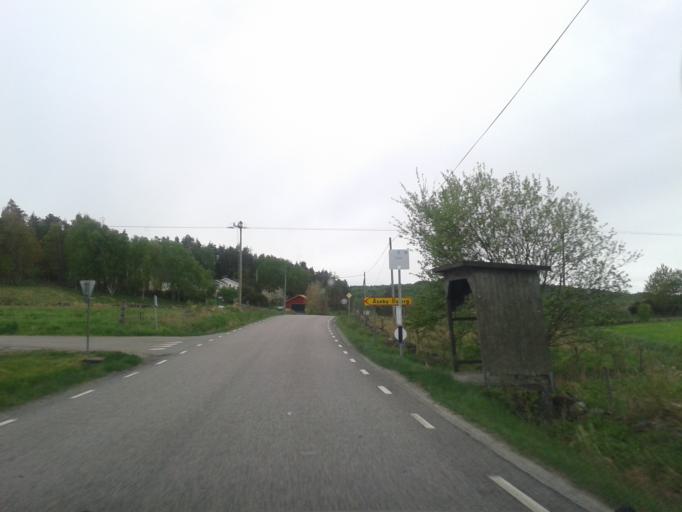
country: SE
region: Vaestra Goetaland
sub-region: Kungalvs Kommun
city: Kode
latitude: 57.9217
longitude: 11.8052
